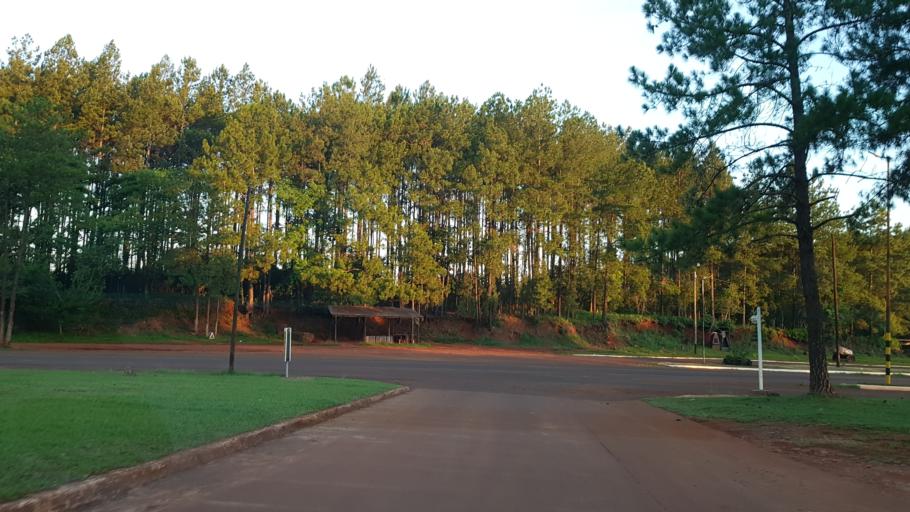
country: AR
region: Misiones
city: Puerto Libertad
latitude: -25.9208
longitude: -54.5753
